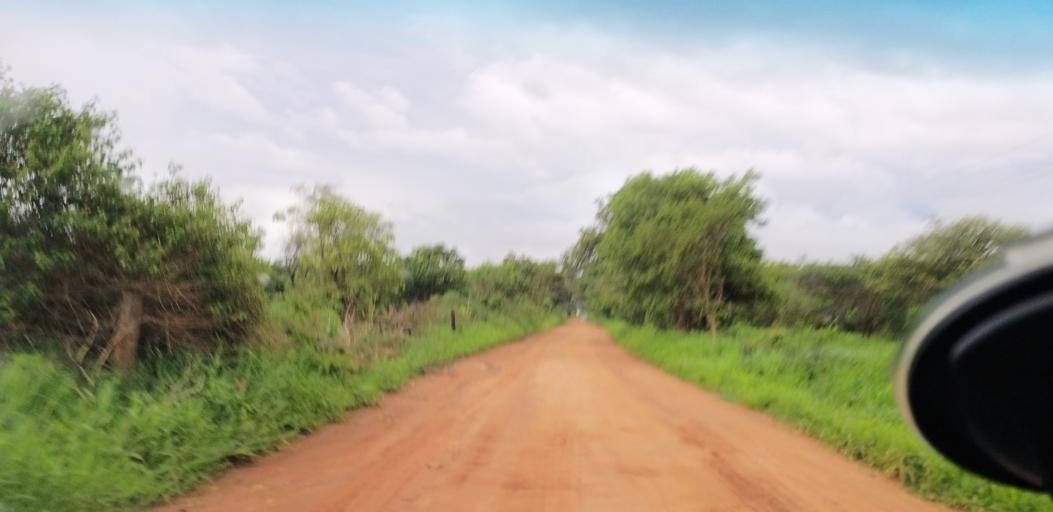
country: ZM
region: Lusaka
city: Lusaka
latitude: -15.5265
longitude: 28.3102
